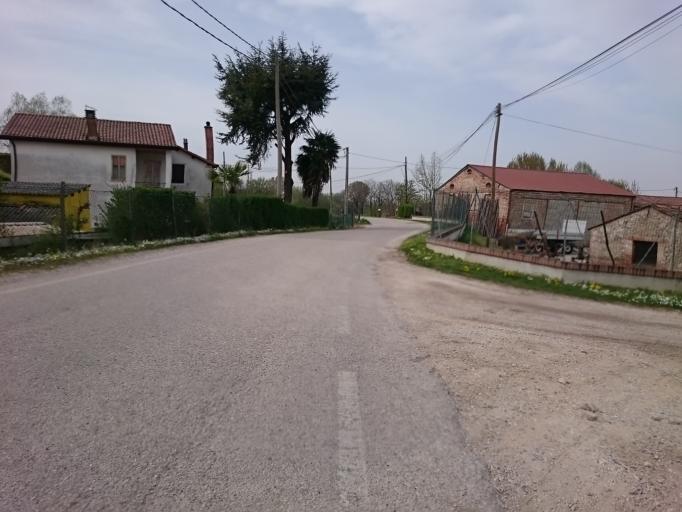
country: IT
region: Veneto
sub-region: Provincia di Padova
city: Anguillara Veneta
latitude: 45.1558
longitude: 11.8558
